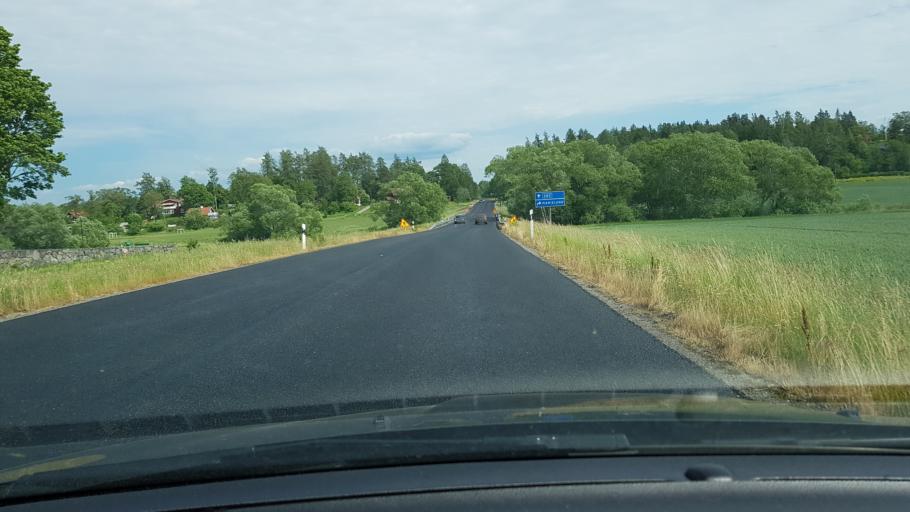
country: SE
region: Uppsala
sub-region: Knivsta Kommun
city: Knivsta
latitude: 59.8554
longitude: 17.8542
